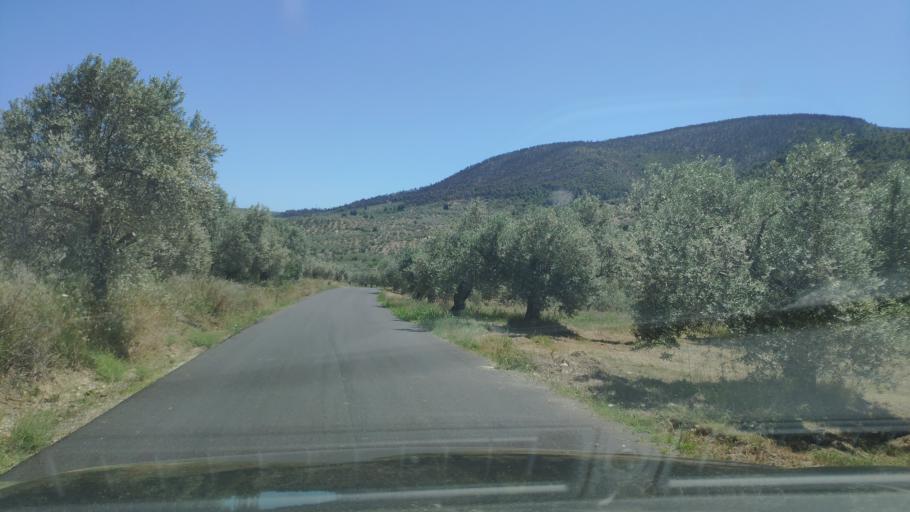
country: GR
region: Peloponnese
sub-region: Nomos Korinthias
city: Athikia
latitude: 37.8060
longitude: 22.9088
